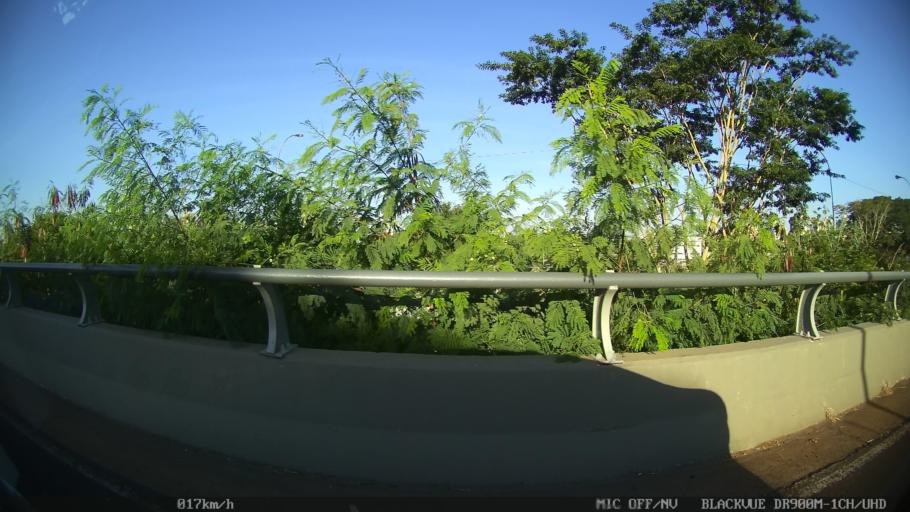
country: BR
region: Sao Paulo
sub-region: Sao Jose Do Rio Preto
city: Sao Jose do Rio Preto
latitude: -20.8050
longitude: -49.3795
